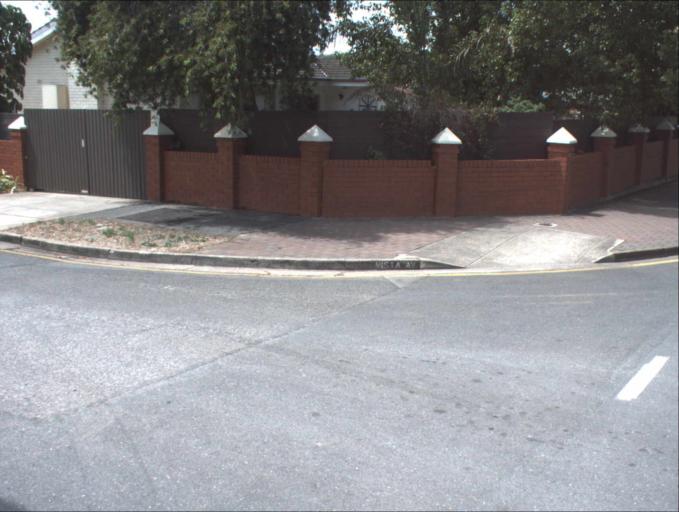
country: AU
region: South Australia
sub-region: Port Adelaide Enfield
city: Gilles Plains
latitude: -34.8456
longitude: 138.6571
